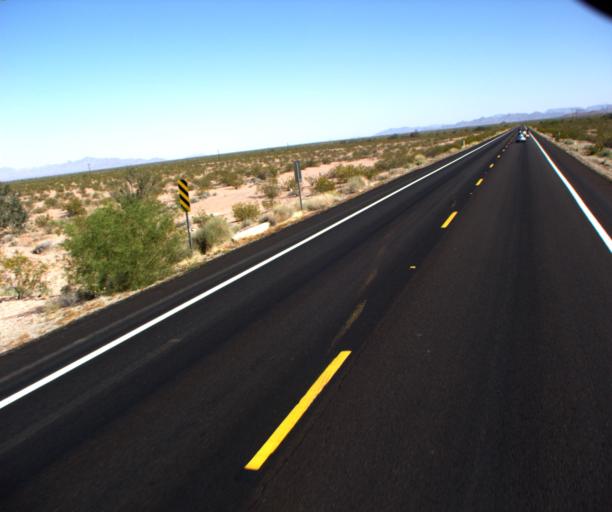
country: US
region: Arizona
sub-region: La Paz County
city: Quartzsite
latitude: 33.2926
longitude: -114.2245
